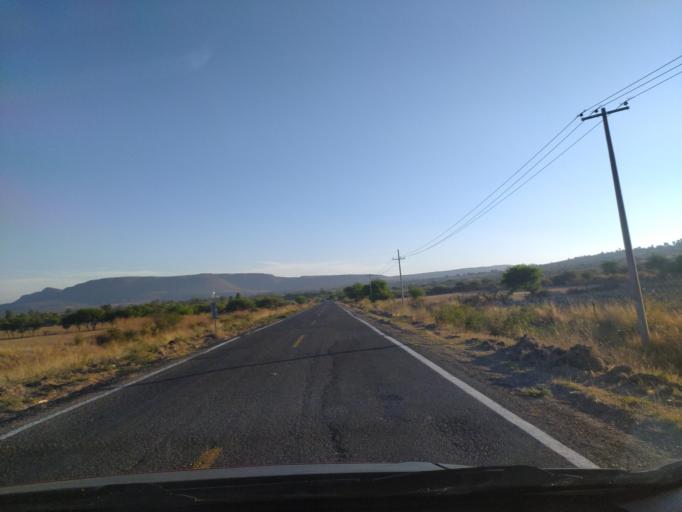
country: MX
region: Guanajuato
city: Ciudad Manuel Doblado
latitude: 20.7396
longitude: -101.8247
